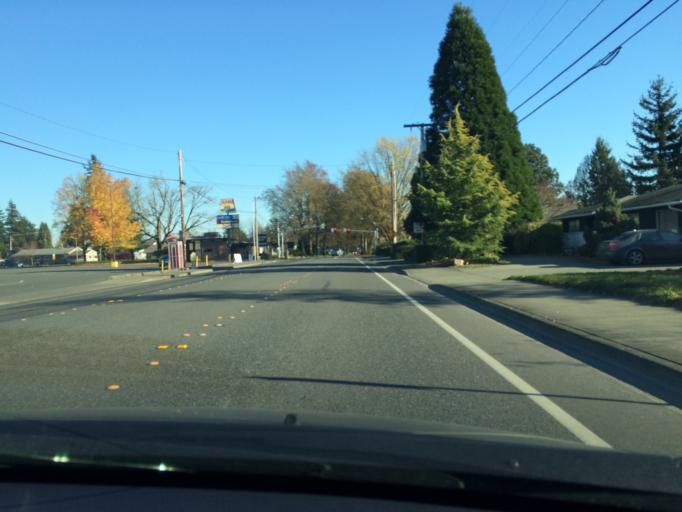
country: US
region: Washington
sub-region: Whatcom County
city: Lynden
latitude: 48.9395
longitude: -122.4710
